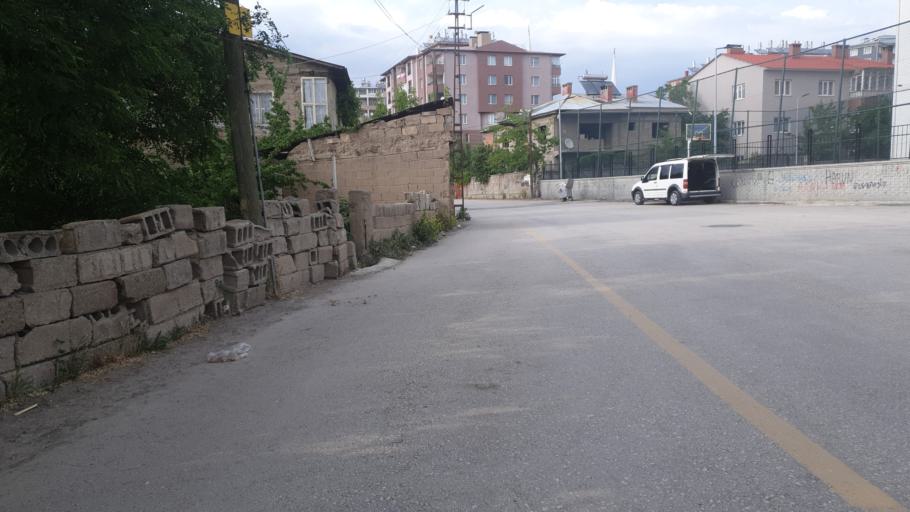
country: TR
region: Van
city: Van
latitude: 38.4903
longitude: 43.3894
